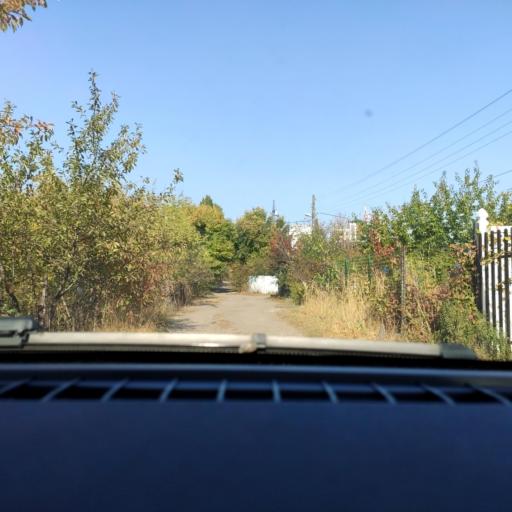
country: RU
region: Voronezj
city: Maslovka
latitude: 51.6078
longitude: 39.2164
